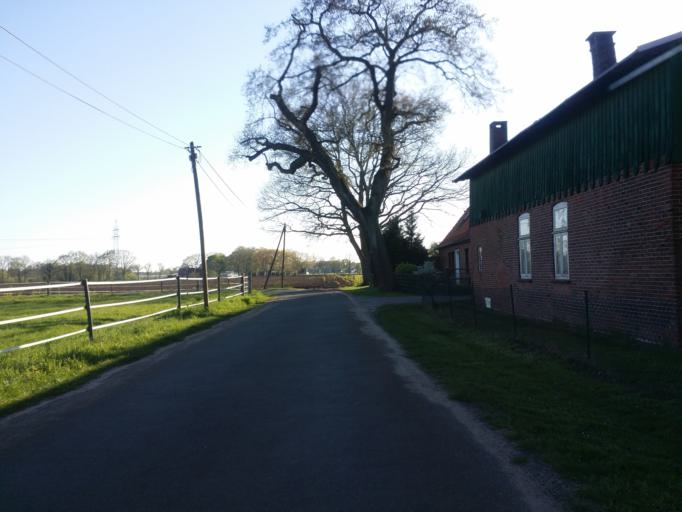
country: DE
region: Lower Saxony
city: Delmenhorst
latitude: 53.0162
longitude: 8.6544
